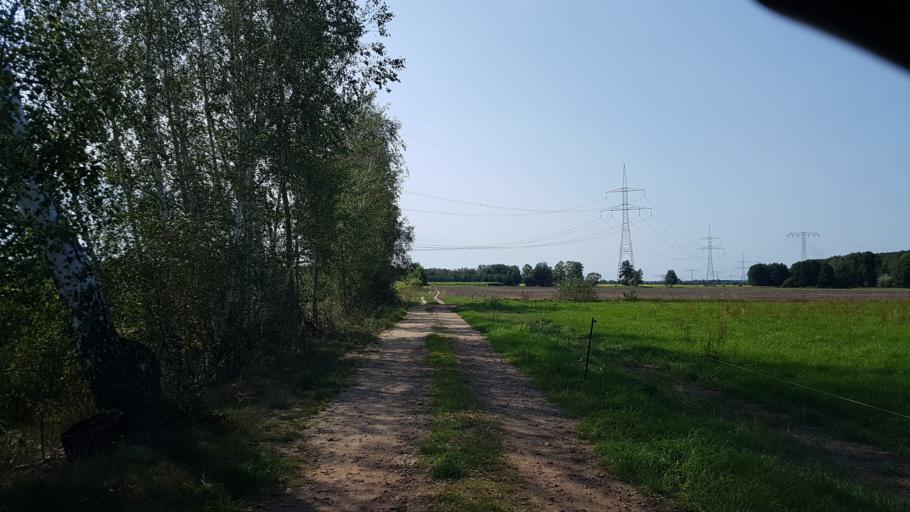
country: DE
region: Brandenburg
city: Schonewalde
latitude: 51.6606
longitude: 13.6295
